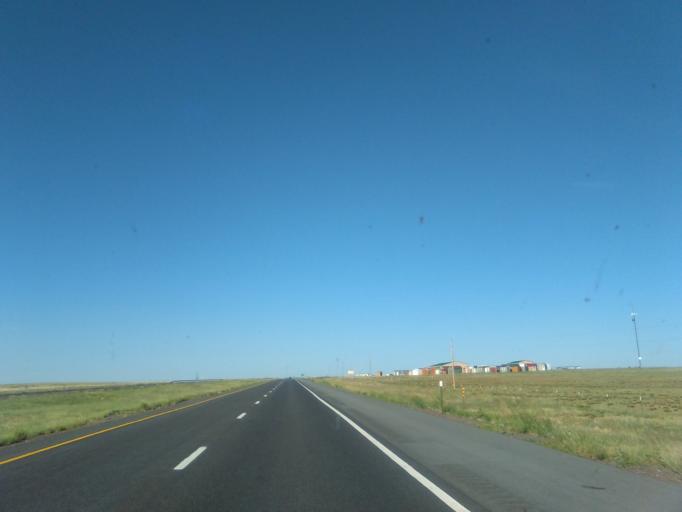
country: US
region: New Mexico
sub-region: San Miguel County
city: Las Vegas
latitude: 35.6913
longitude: -105.1278
